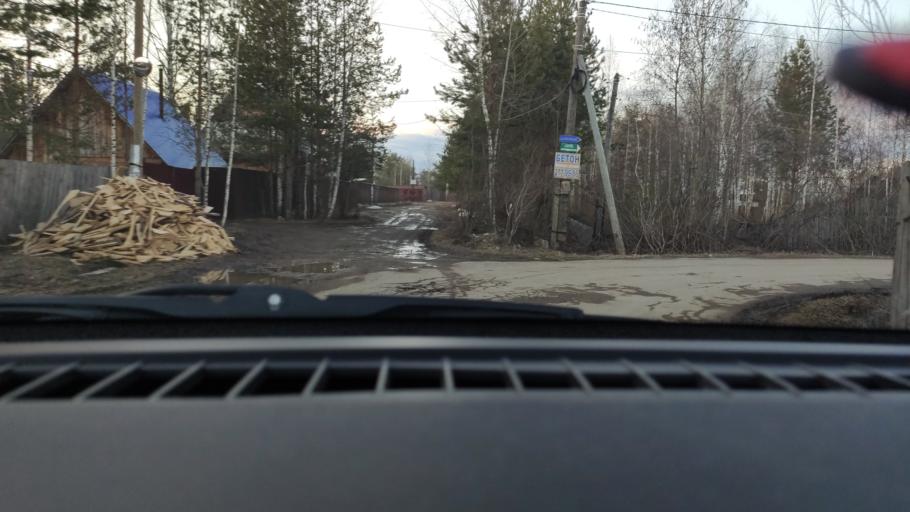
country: RU
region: Perm
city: Perm
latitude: 58.0819
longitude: 56.3137
